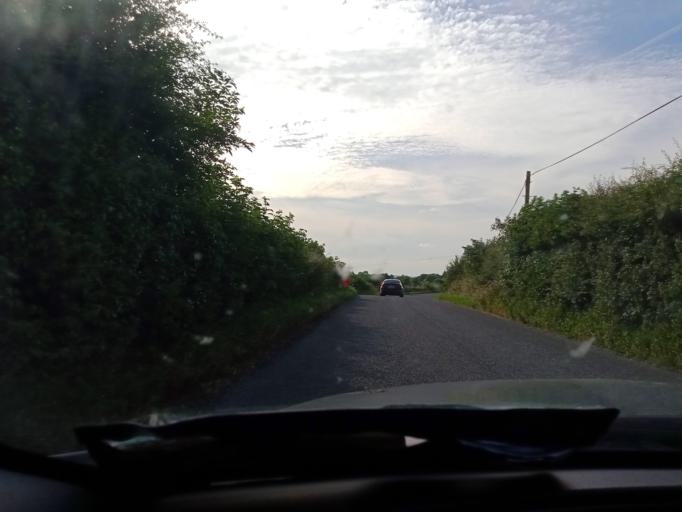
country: IE
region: Leinster
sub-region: An Iarmhi
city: Castlepollard
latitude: 53.7117
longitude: -7.3169
